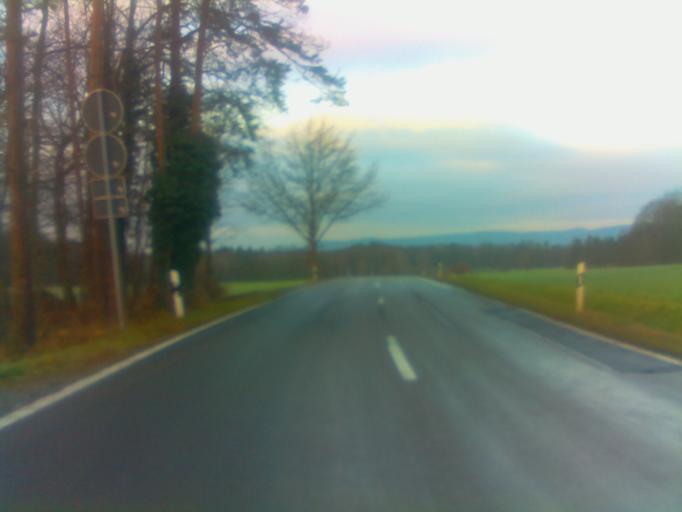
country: DE
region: Thuringia
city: Hummelshain
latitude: 50.7682
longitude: 11.6155
